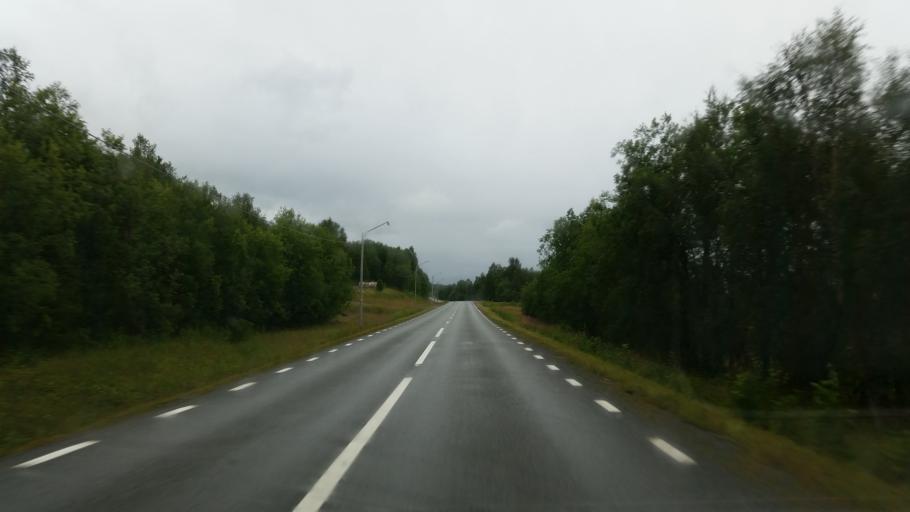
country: NO
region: Nordland
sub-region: Rana
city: Mo i Rana
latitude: 65.8636
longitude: 15.0218
